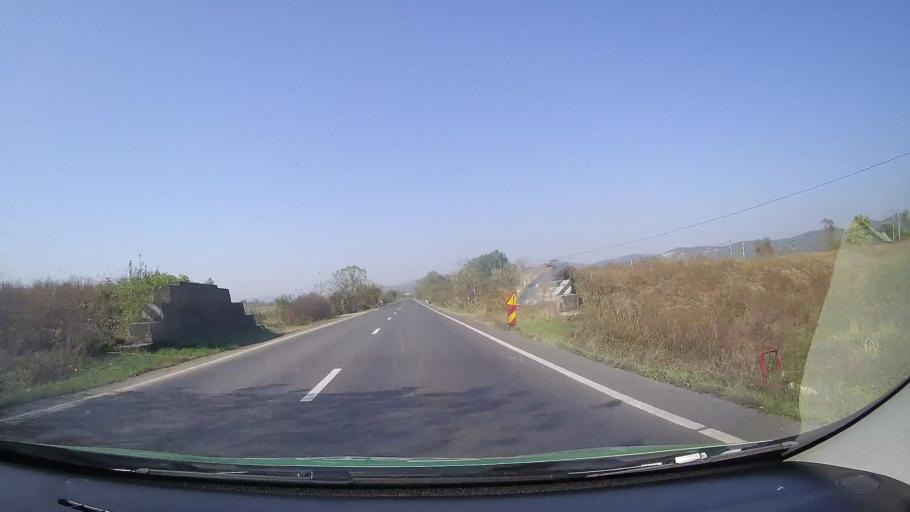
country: RO
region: Hunedoara
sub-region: Comuna Ilia
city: Ilia
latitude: 45.9412
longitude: 22.6410
